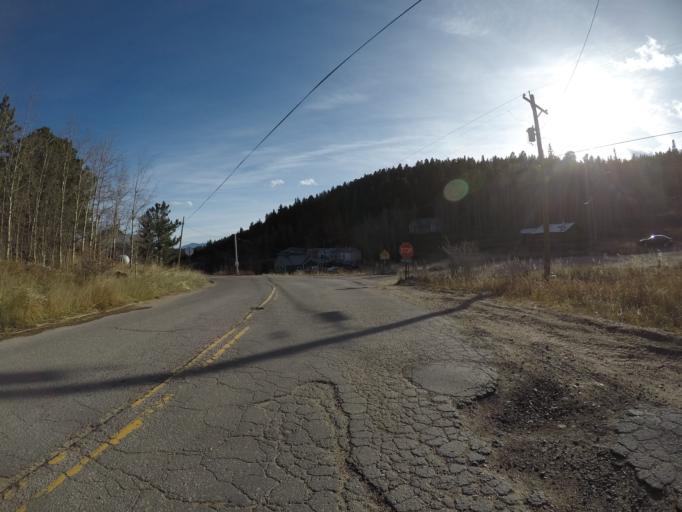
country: US
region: Colorado
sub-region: Boulder County
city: Nederland
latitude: 40.0722
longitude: -105.5073
